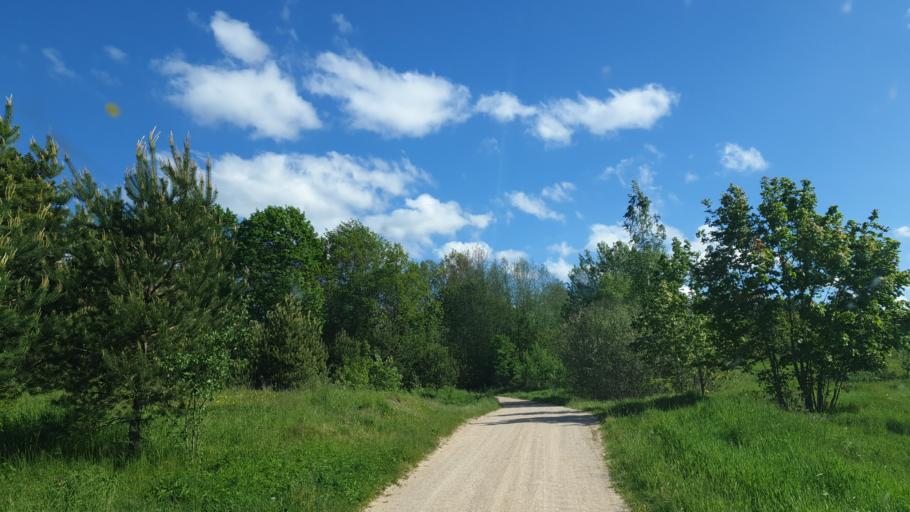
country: LT
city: Aukstadvaris
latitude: 54.5793
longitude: 24.4598
